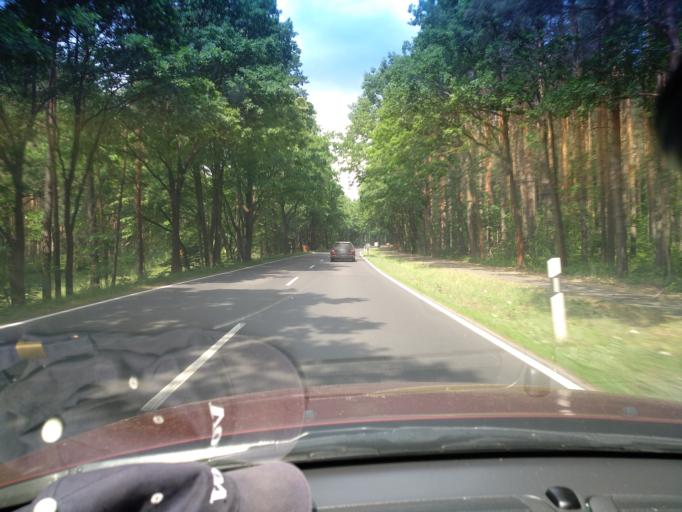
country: DE
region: Saxony
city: Niesky
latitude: 51.2834
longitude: 14.8118
